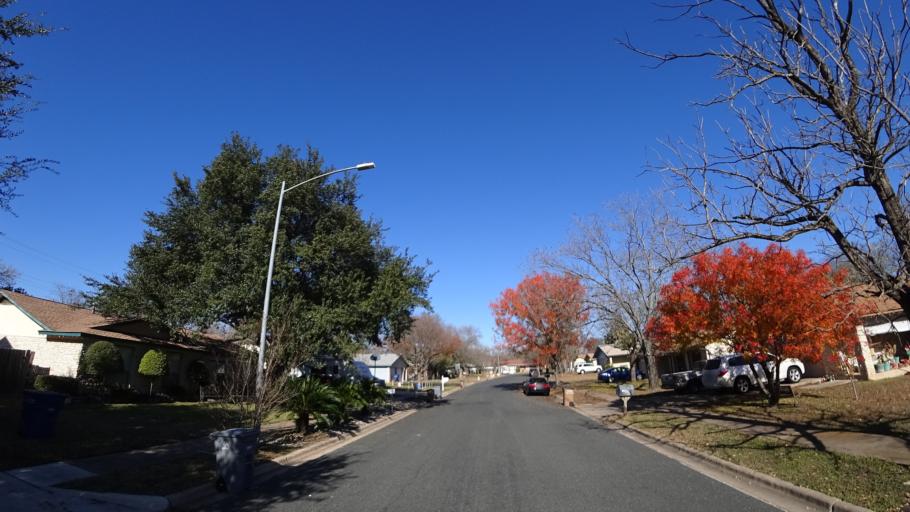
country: US
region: Texas
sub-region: Travis County
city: Wells Branch
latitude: 30.4195
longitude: -97.6966
